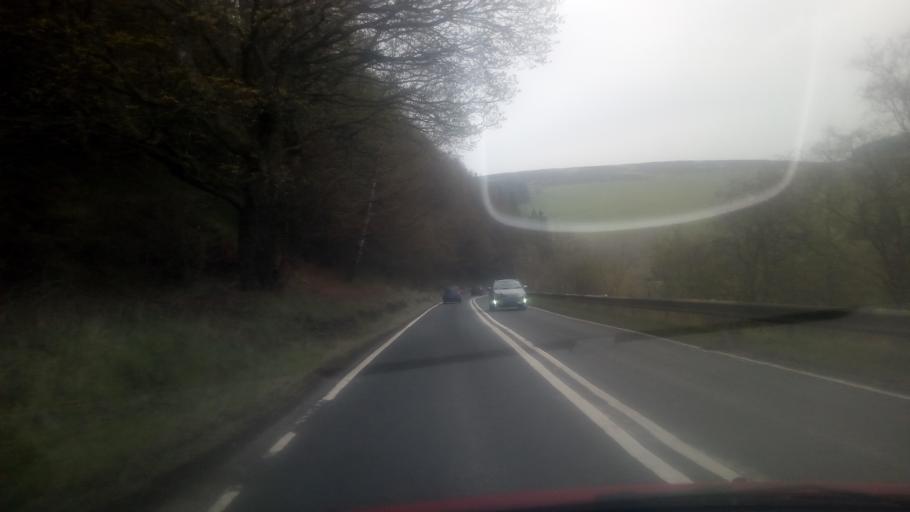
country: GB
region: Scotland
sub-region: The Scottish Borders
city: Galashiels
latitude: 55.7058
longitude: -2.8868
